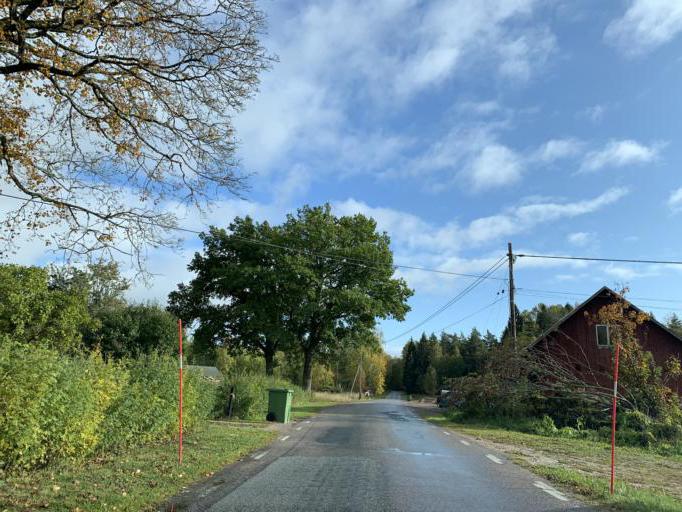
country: SE
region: Soedermanland
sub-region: Eskilstuna Kommun
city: Kvicksund
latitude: 59.3298
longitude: 16.2558
